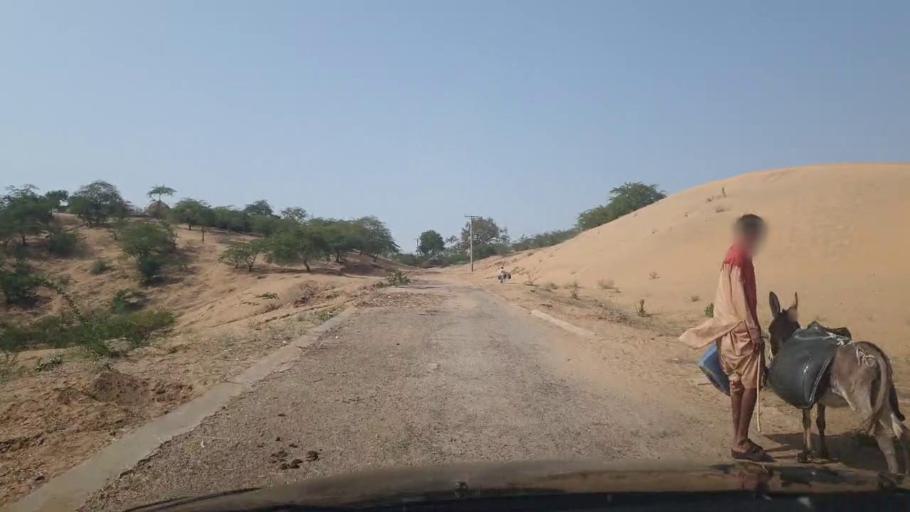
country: PK
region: Sindh
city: Islamkot
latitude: 24.9996
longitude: 70.2062
